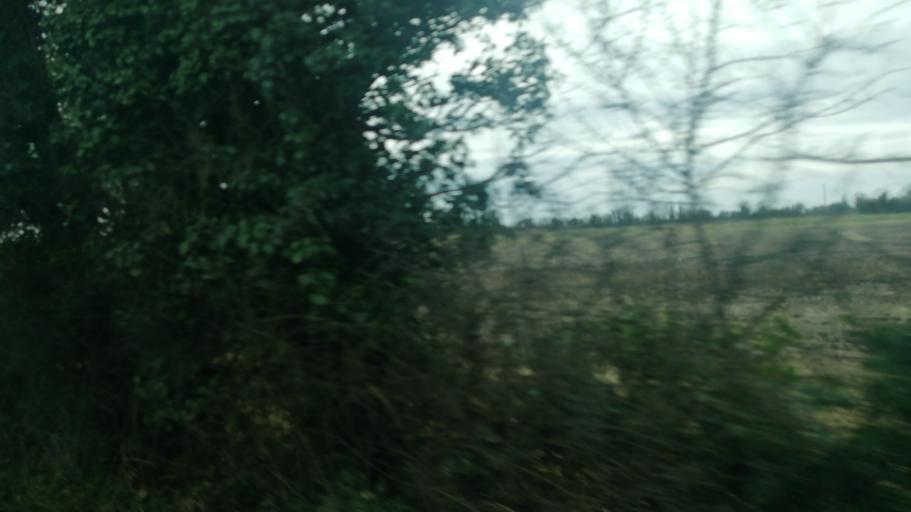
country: IE
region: Leinster
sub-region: Kildare
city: Derrinturn
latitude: 53.2921
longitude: -6.8996
